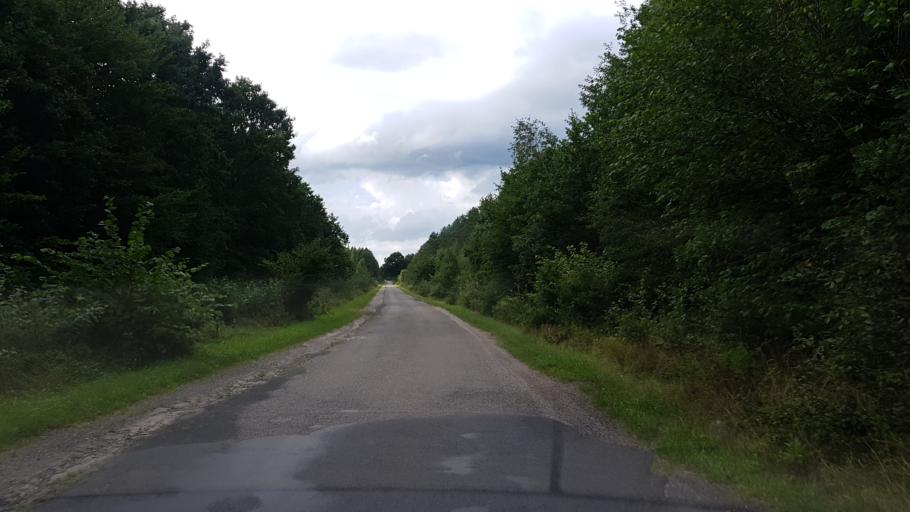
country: PL
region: West Pomeranian Voivodeship
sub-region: Powiat bialogardzki
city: Tychowo
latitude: 54.0287
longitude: 16.3529
